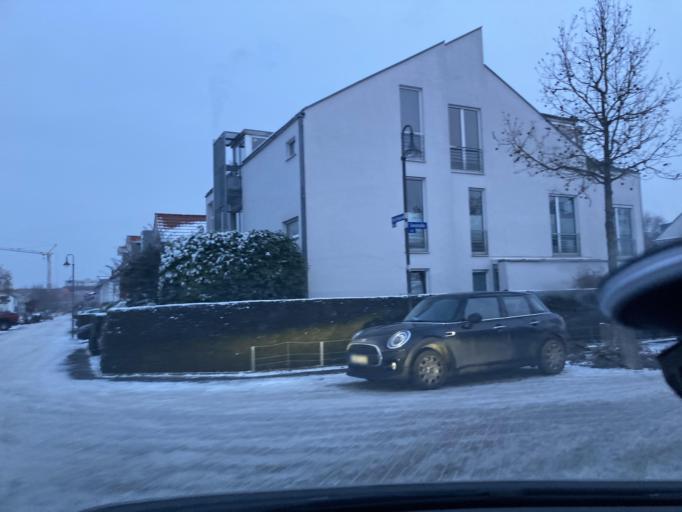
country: DE
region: Hesse
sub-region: Regierungsbezirk Darmstadt
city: Offenbach
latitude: 50.1262
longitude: 8.7841
